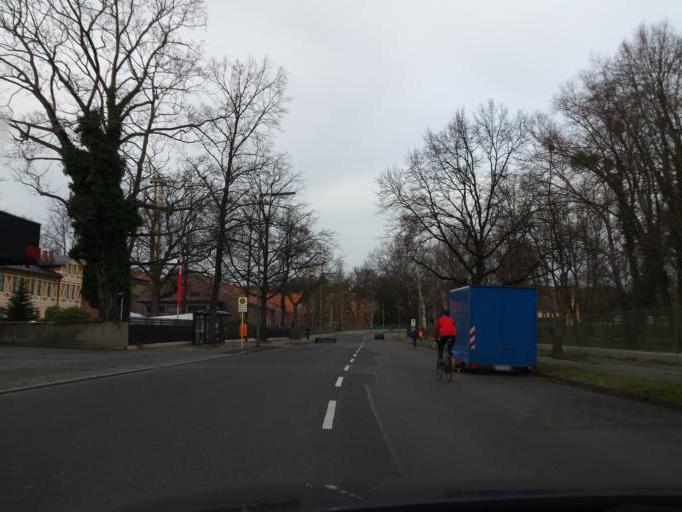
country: DE
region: Berlin
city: Nikolassee
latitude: 52.4294
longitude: 13.1850
